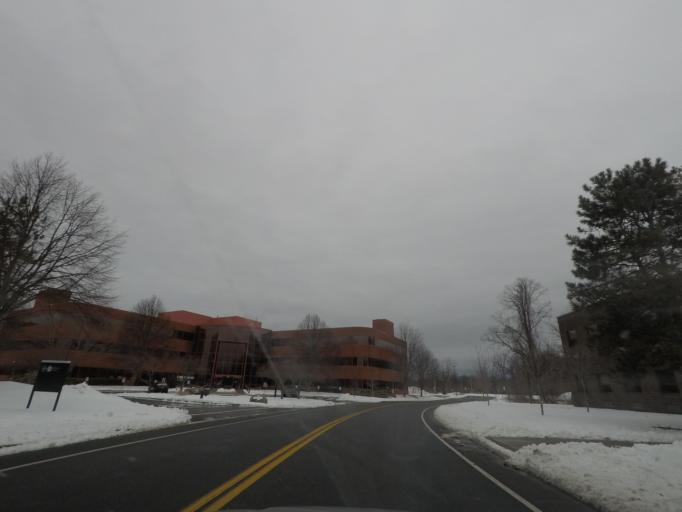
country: US
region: New York
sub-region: Albany County
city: Roessleville
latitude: 42.7195
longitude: -73.7983
